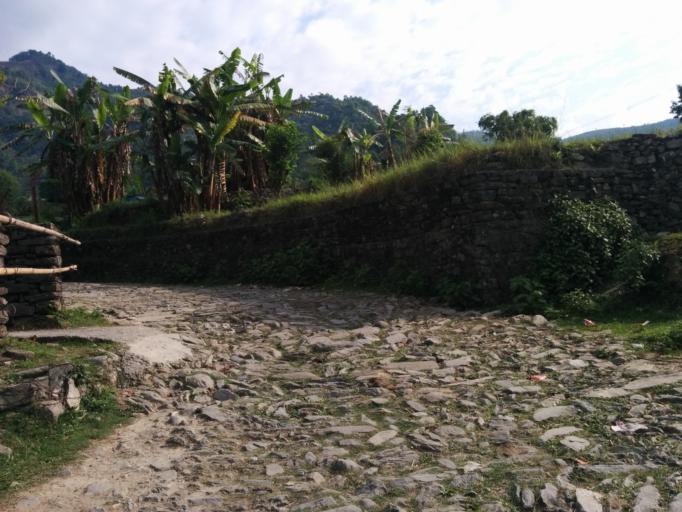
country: NP
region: Western Region
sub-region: Gandaki Zone
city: Pokhara
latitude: 28.2260
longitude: 83.9507
